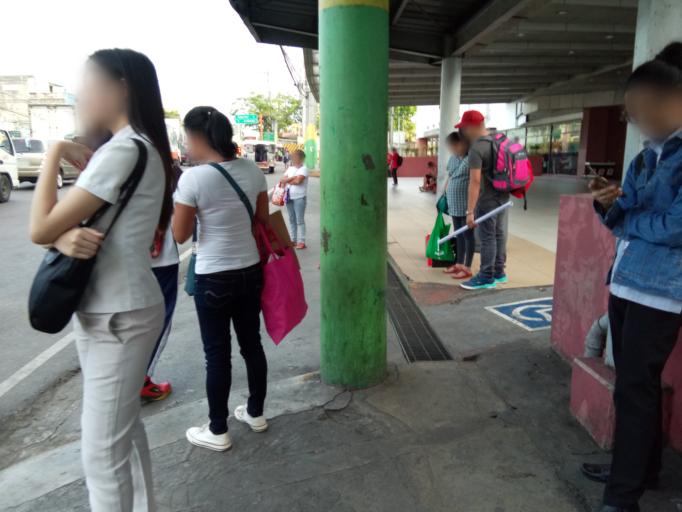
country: PH
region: Calabarzon
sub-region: Province of Cavite
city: Dasmarinas
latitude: 14.2998
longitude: 120.9544
